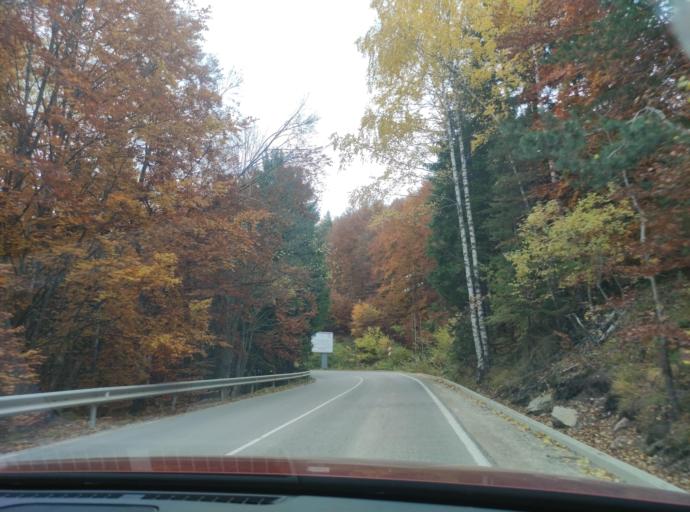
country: BG
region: Sofiya
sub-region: Obshtina Godech
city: Godech
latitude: 43.1103
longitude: 23.1114
